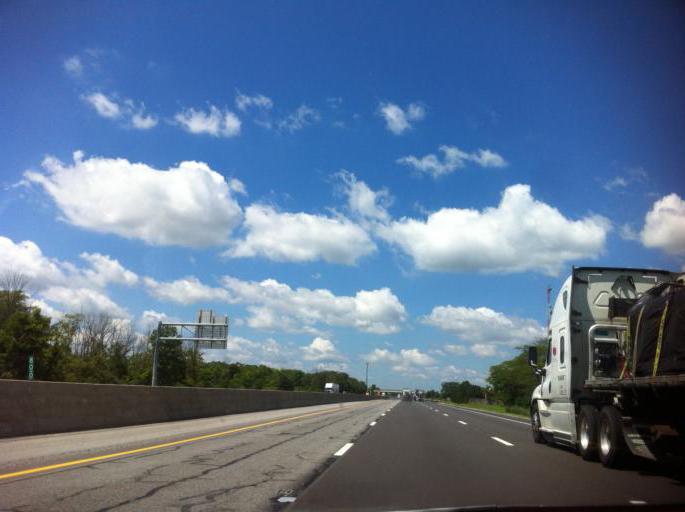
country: US
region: Ohio
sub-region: Ottawa County
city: Elmore
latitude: 41.4696
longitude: -83.3167
